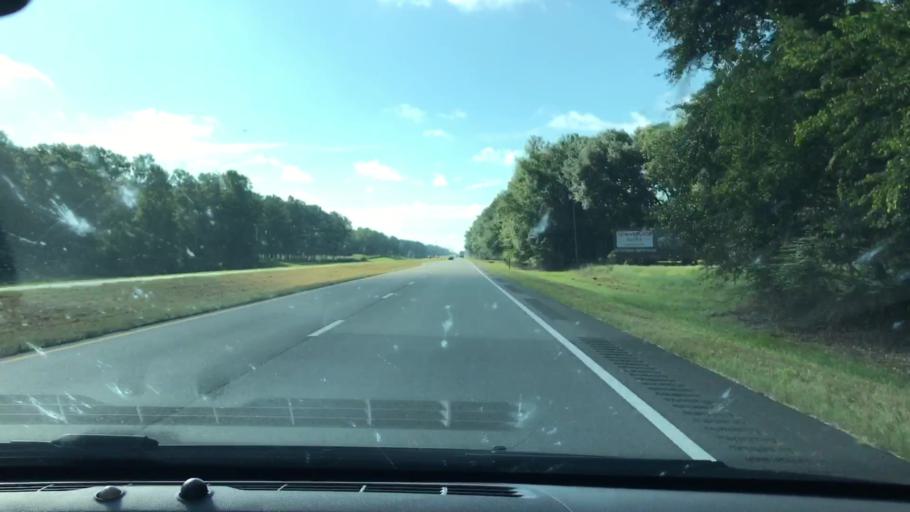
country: US
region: Georgia
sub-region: Lee County
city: Leesburg
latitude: 31.6809
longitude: -84.3005
